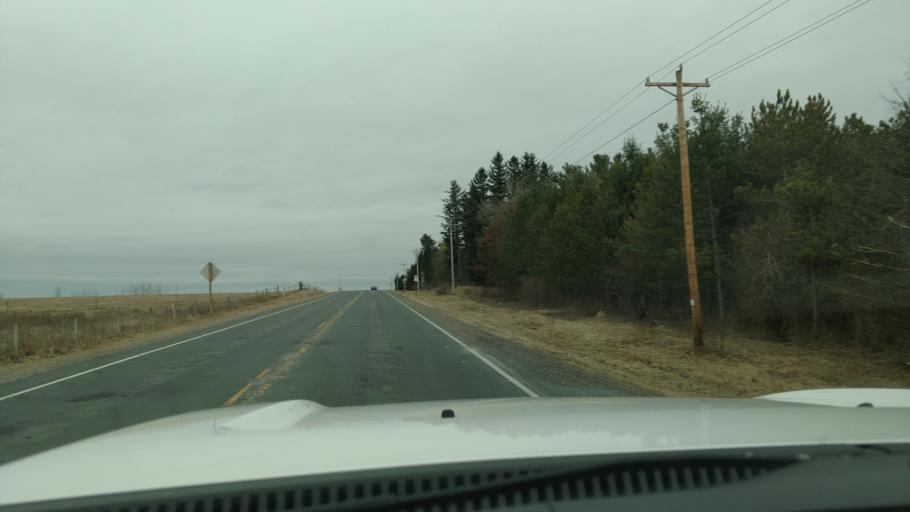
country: US
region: Wisconsin
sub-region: Saint Croix County
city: Hammond
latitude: 44.9377
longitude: -92.4357
